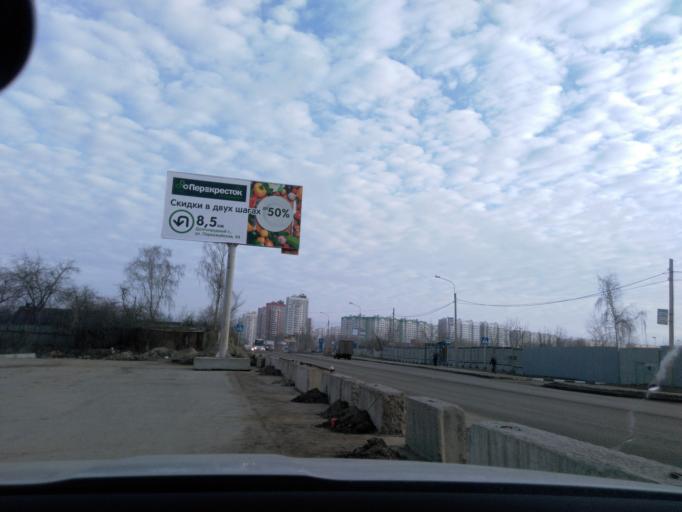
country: RU
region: Moskovskaya
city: Dolgoprudnyy
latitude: 55.9254
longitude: 37.4927
